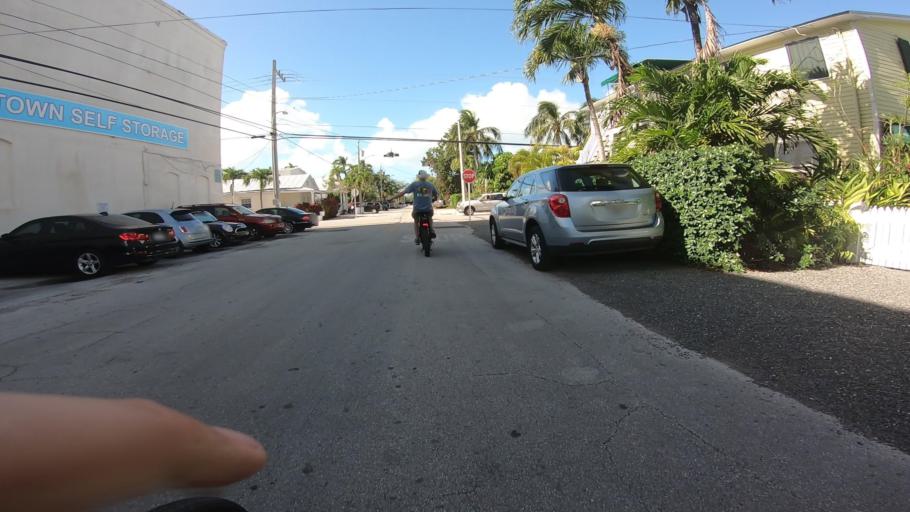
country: US
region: Florida
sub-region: Monroe County
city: Key West
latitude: 24.5527
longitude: -81.7917
